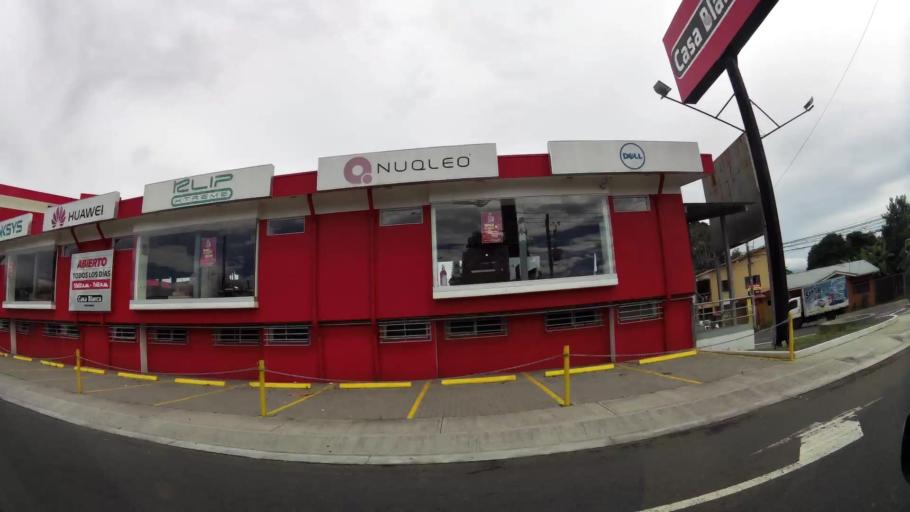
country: CR
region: San Jose
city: San Pedro
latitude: 9.9197
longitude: -84.0516
